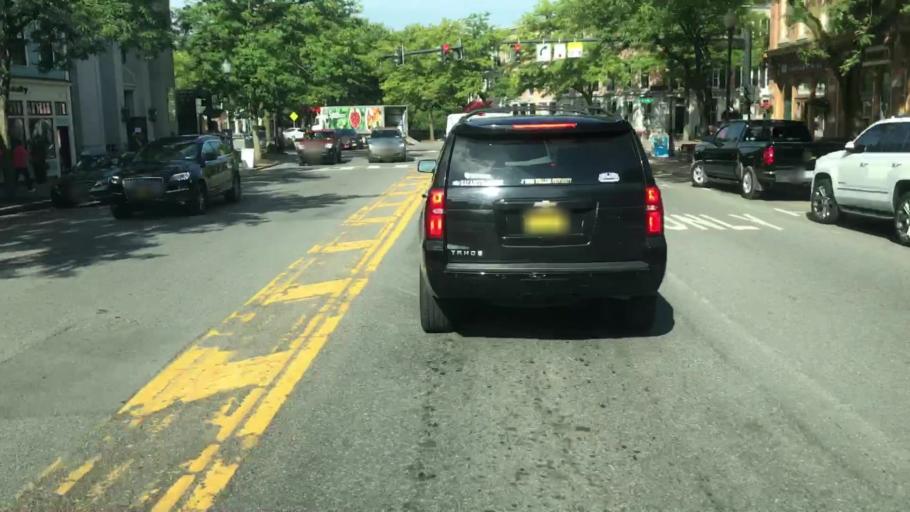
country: US
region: New York
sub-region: Onondaga County
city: Skaneateles
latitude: 42.9458
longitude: -76.4285
